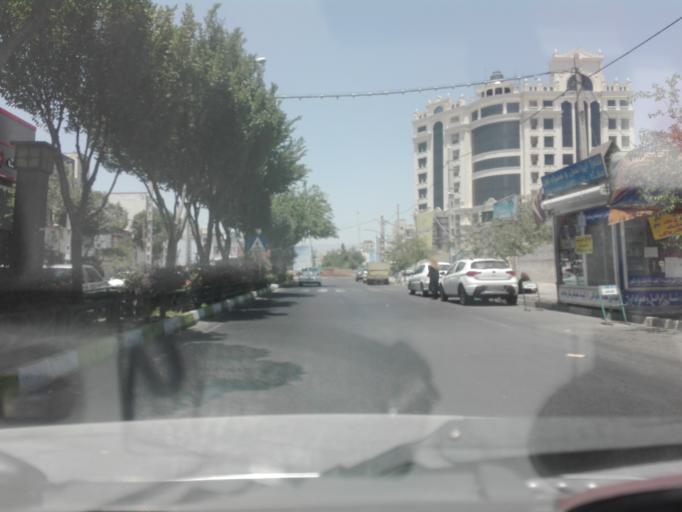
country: IR
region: Tehran
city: Shahre Jadide Andisheh
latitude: 35.7323
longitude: 50.9905
